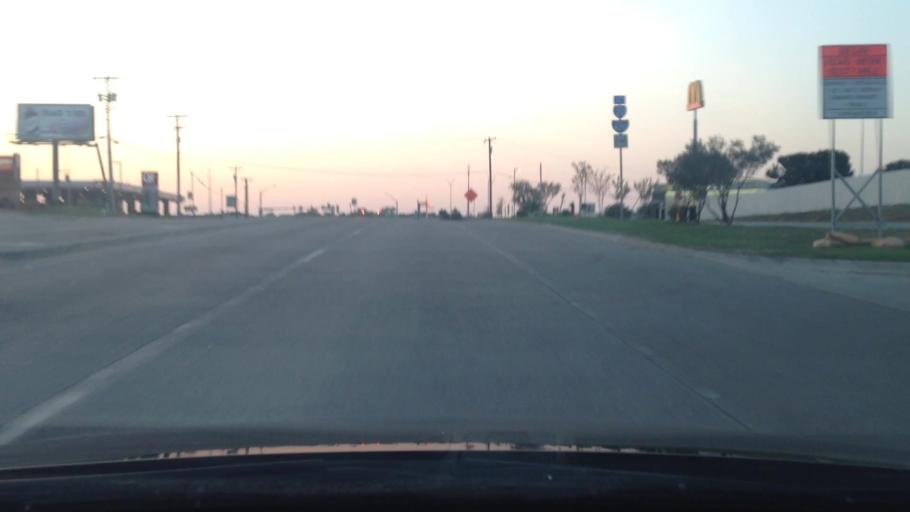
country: US
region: Texas
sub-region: Tarrant County
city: Kennedale
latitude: 32.6636
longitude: -97.2393
